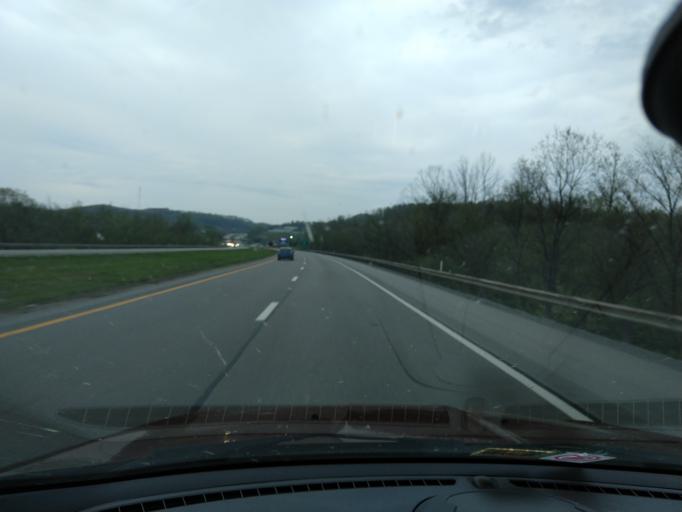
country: US
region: West Virginia
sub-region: Lewis County
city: Weston
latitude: 39.0943
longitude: -80.3924
